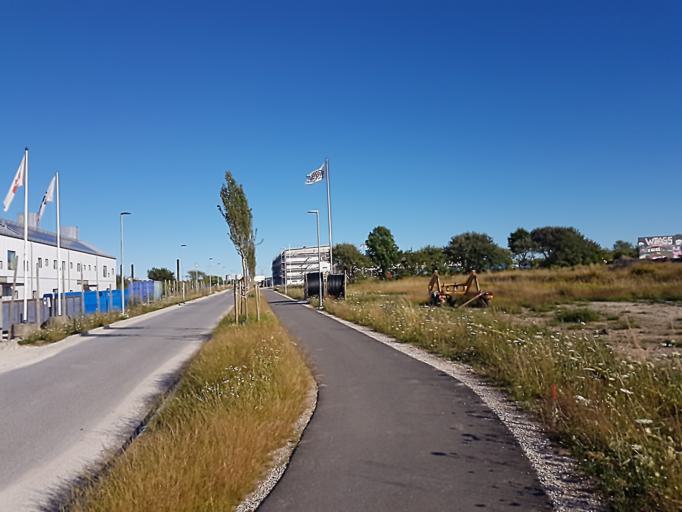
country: SE
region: Gotland
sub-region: Gotland
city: Visby
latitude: 57.6282
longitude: 18.3088
